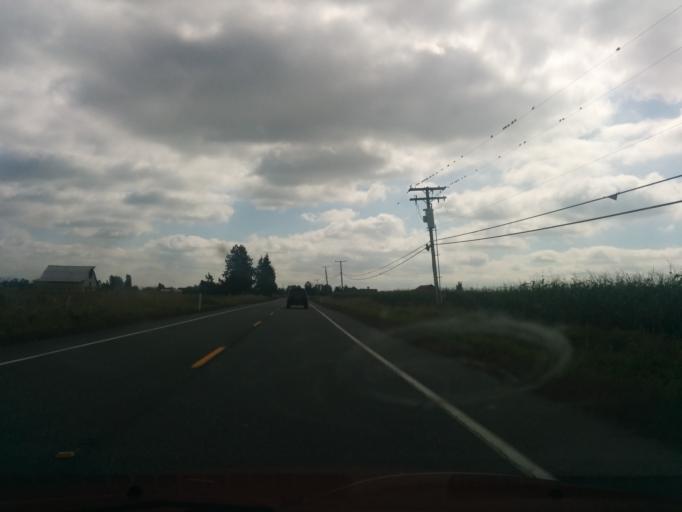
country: US
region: Washington
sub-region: Skagit County
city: Burlington
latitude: 48.5756
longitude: -122.4222
